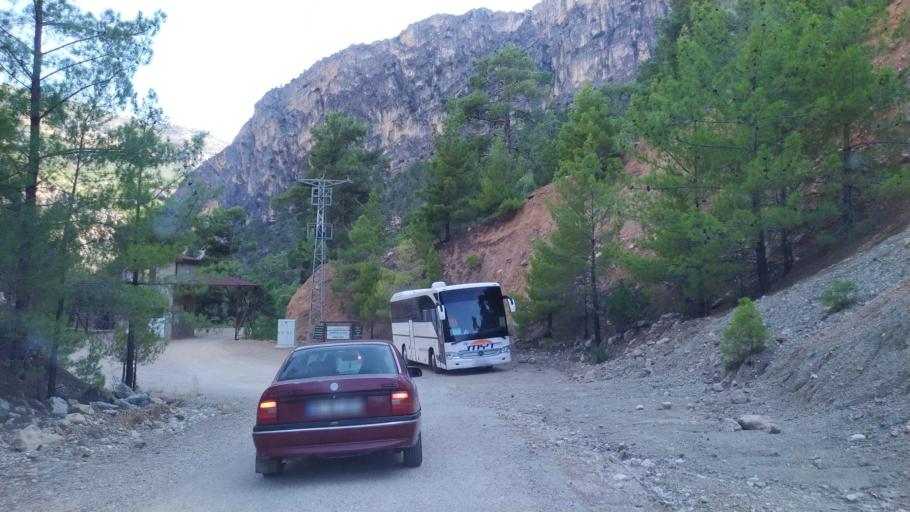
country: TR
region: Mersin
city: Mut
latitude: 36.5436
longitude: 33.2327
